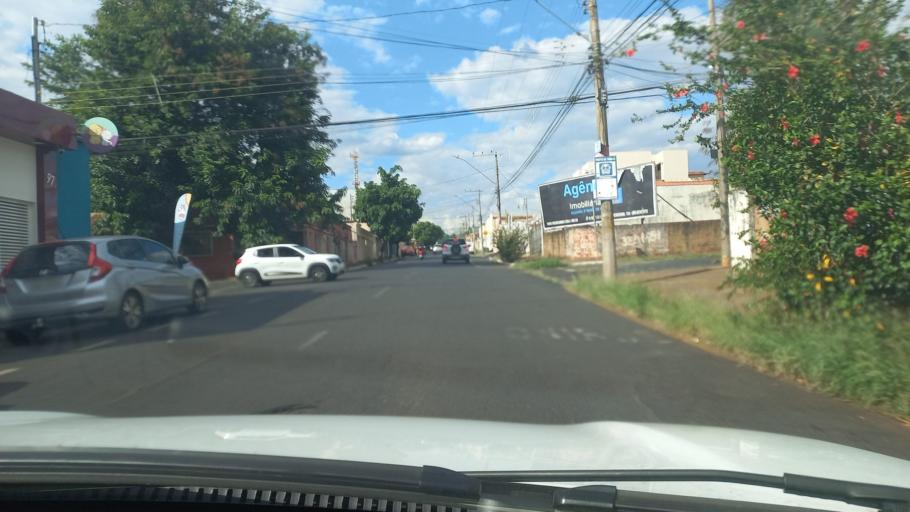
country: BR
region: Minas Gerais
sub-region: Uberaba
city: Uberaba
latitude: -19.7400
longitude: -47.9290
